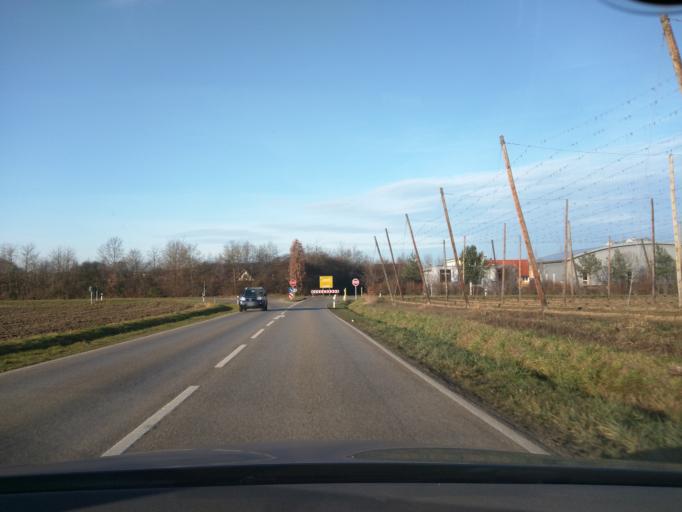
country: DE
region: Bavaria
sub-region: Upper Bavaria
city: Rohrbach
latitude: 48.6068
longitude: 11.5811
